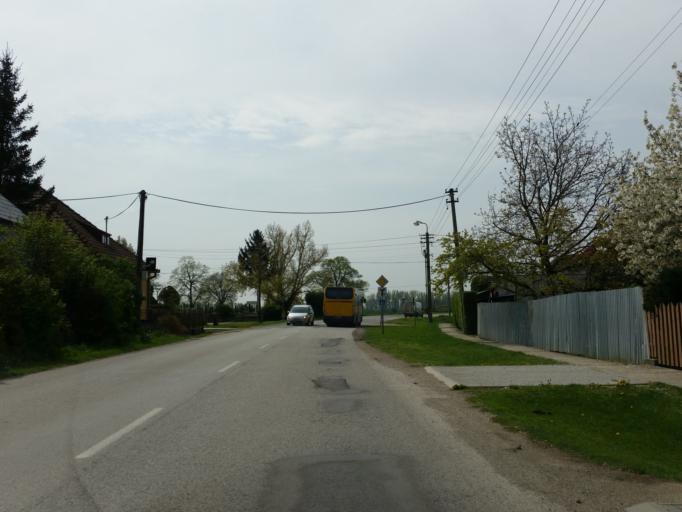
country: SK
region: Trnavsky
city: Leopoldov
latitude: 48.3752
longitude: 17.7468
